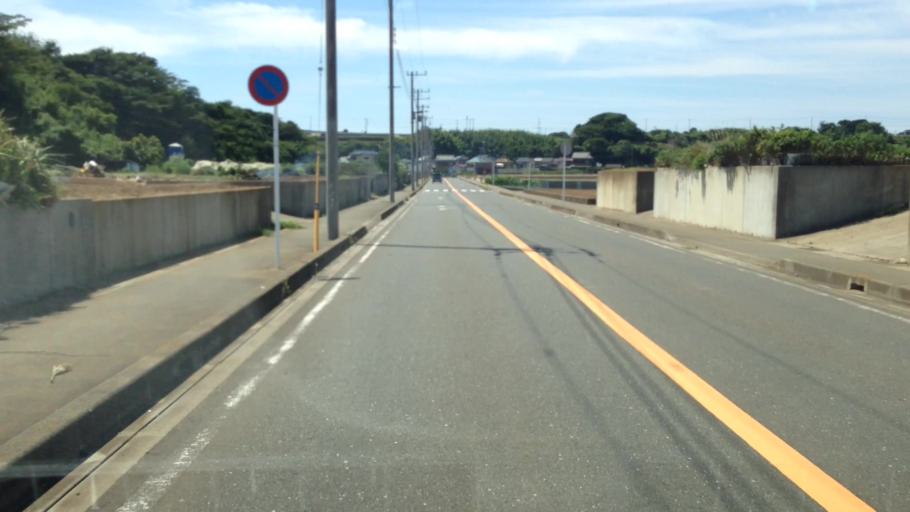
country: JP
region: Kanagawa
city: Miura
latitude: 35.1996
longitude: 139.6232
